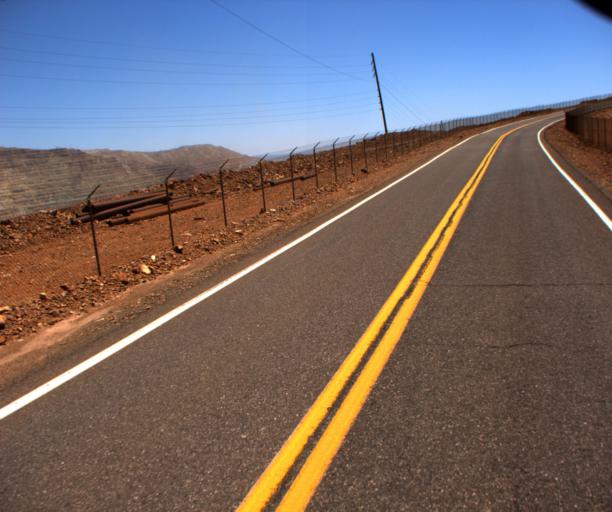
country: US
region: Arizona
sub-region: Greenlee County
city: Morenci
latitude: 33.1135
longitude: -109.3747
